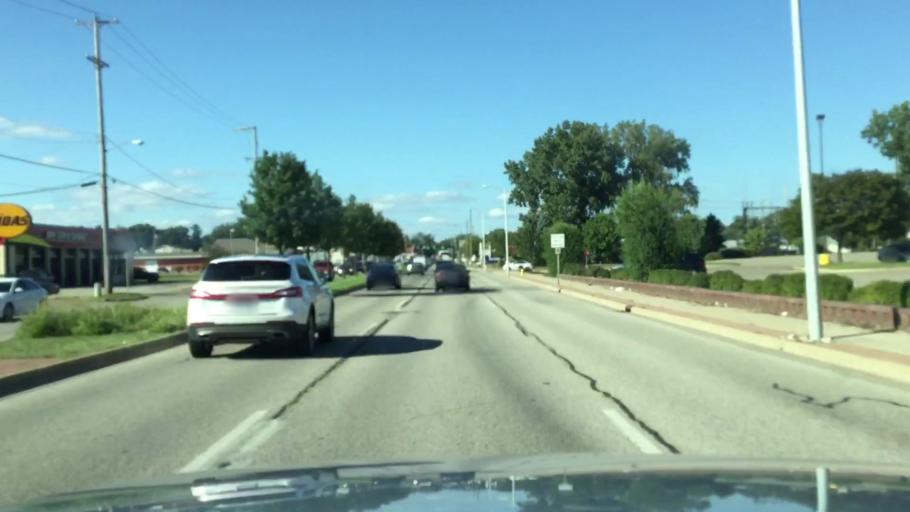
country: US
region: Michigan
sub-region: Kalamazoo County
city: Portage
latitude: 42.2423
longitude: -85.5895
